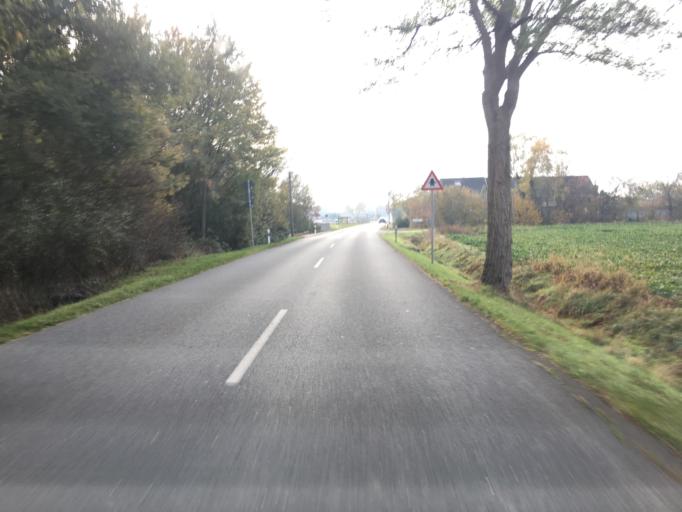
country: DE
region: North Rhine-Westphalia
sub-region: Regierungsbezirk Dusseldorf
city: Sonsbeck
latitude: 51.6101
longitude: 6.3664
